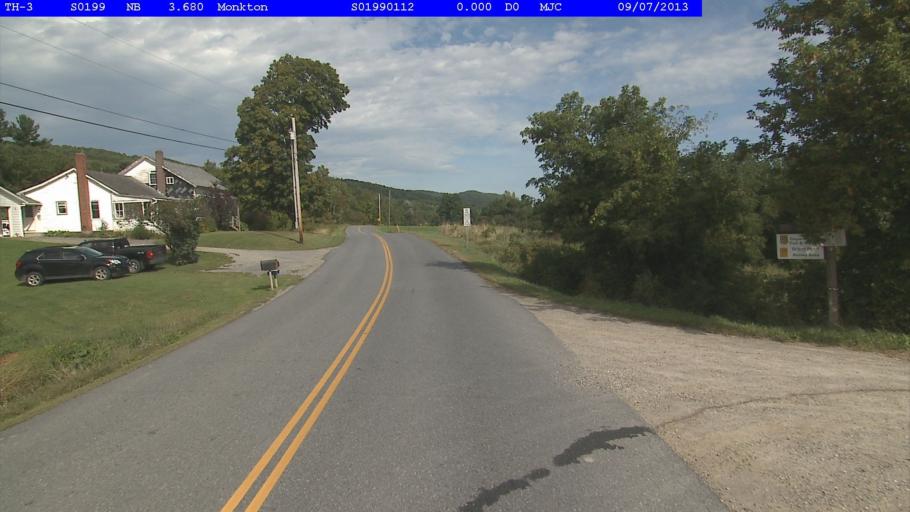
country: US
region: Vermont
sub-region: Addison County
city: Bristol
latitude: 44.1810
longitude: -73.1041
